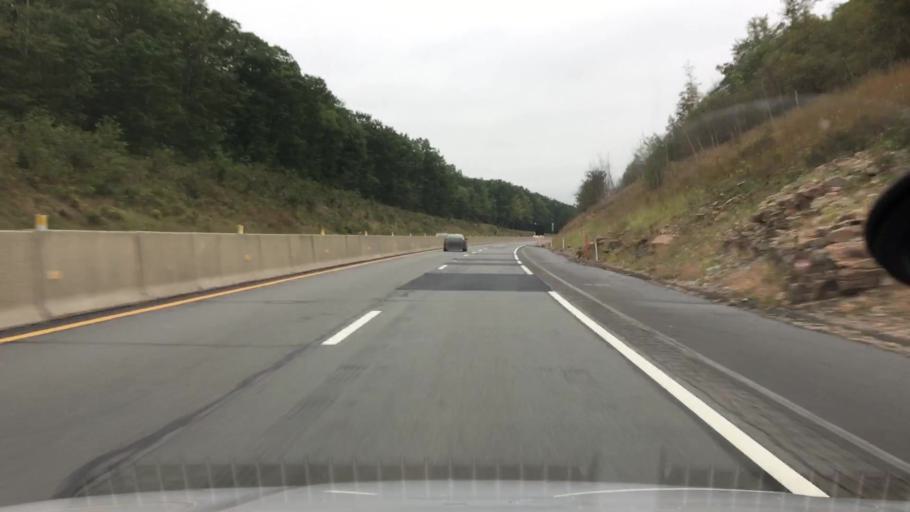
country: US
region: Pennsylvania
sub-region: Luzerne County
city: White Haven
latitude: 41.0791
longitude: -75.7301
